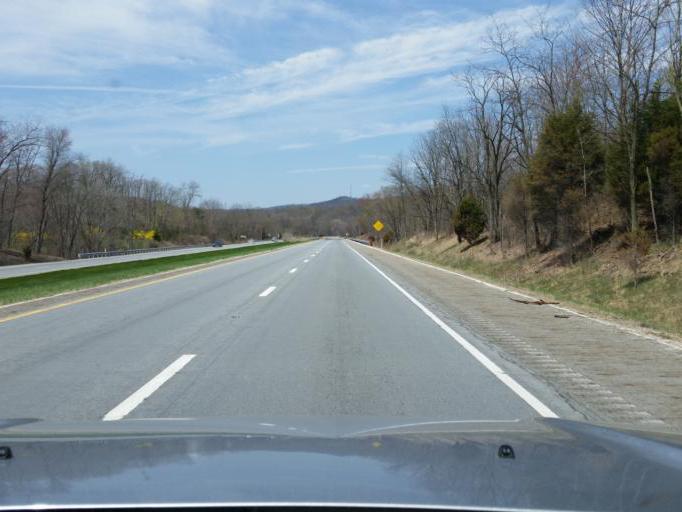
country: US
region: Pennsylvania
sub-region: Perry County
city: Newport
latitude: 40.5355
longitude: -77.1410
